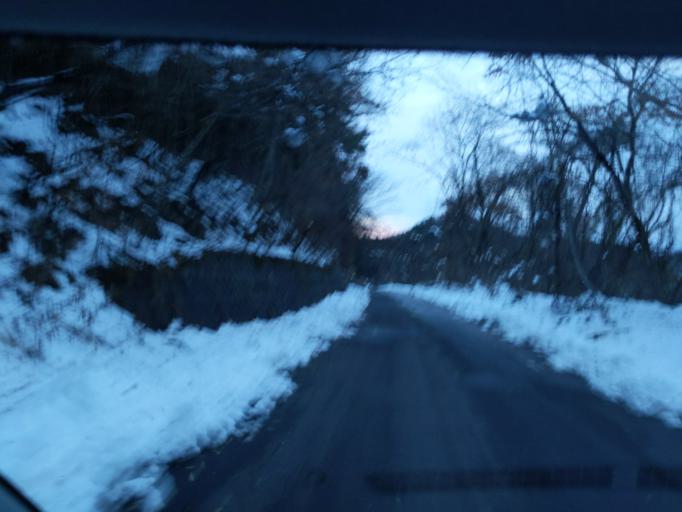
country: JP
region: Iwate
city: Mizusawa
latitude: 39.0501
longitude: 141.0220
